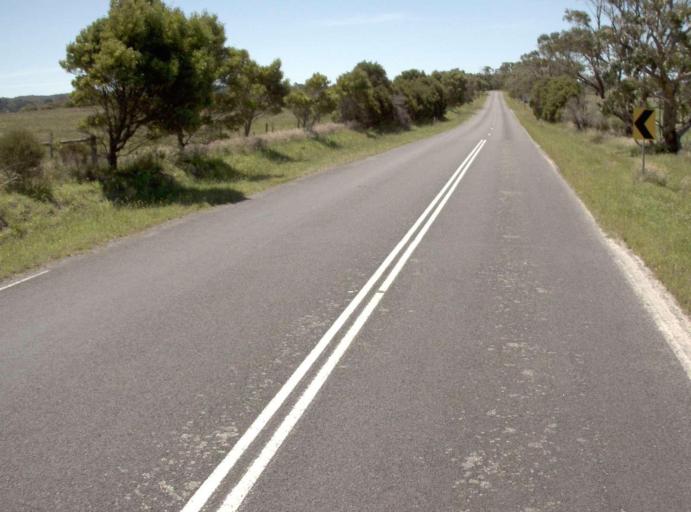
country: AU
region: Victoria
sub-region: Bass Coast
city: North Wonthaggi
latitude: -38.7902
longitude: 146.0868
